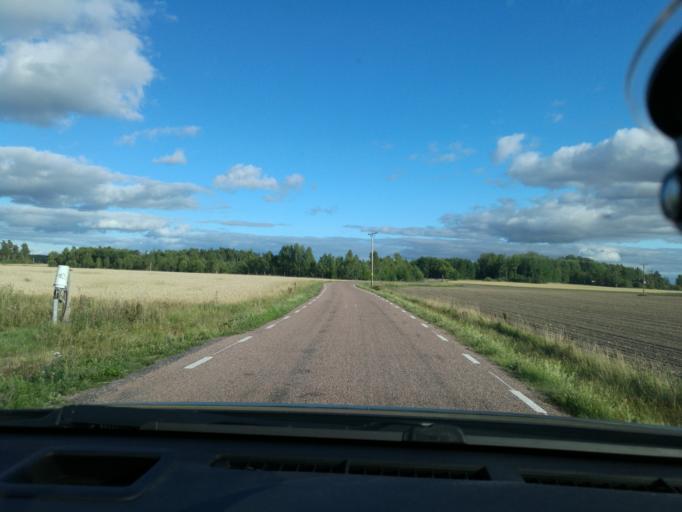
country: SE
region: Vaestmanland
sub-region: Hallstahammars Kommun
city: Hallstahammar
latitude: 59.5442
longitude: 16.1270
